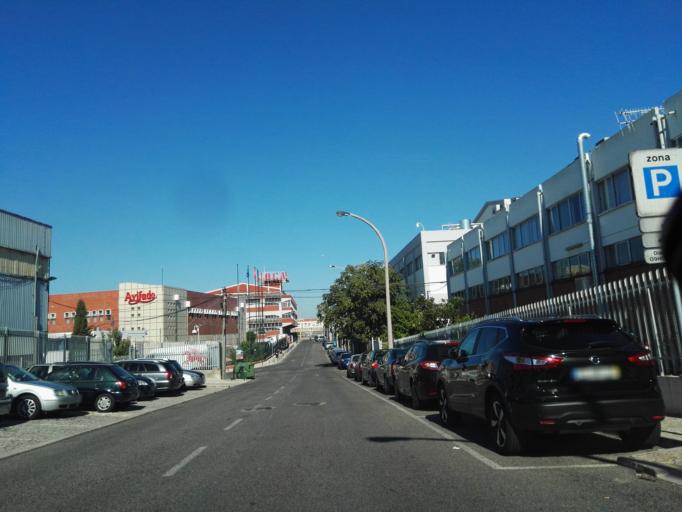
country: PT
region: Lisbon
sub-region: Loures
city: Camarate
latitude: 38.7865
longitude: -9.1257
